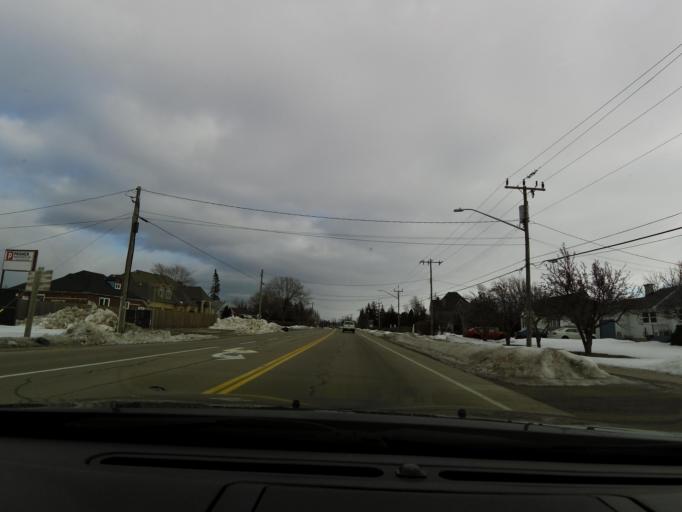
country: CA
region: Ontario
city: Hamilton
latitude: 43.2076
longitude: -79.6506
